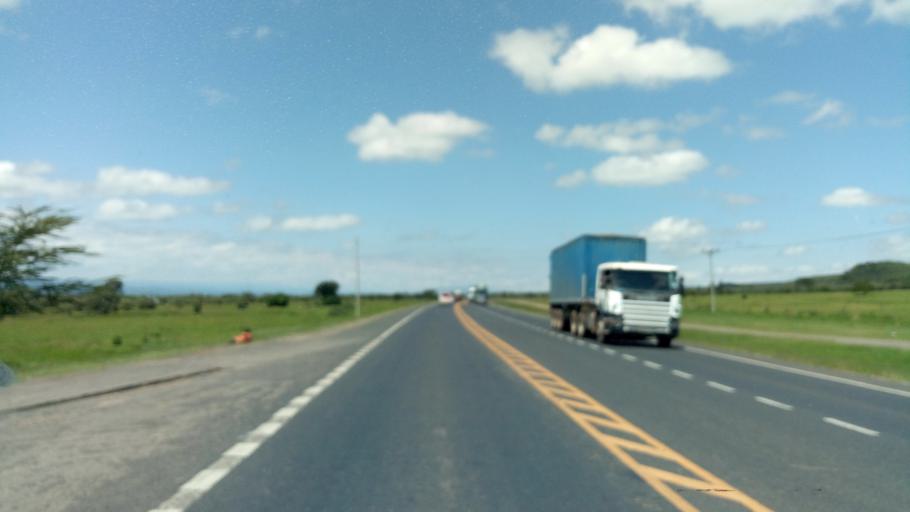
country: KE
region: Nakuru
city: Naivasha
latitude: -0.5277
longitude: 36.3315
